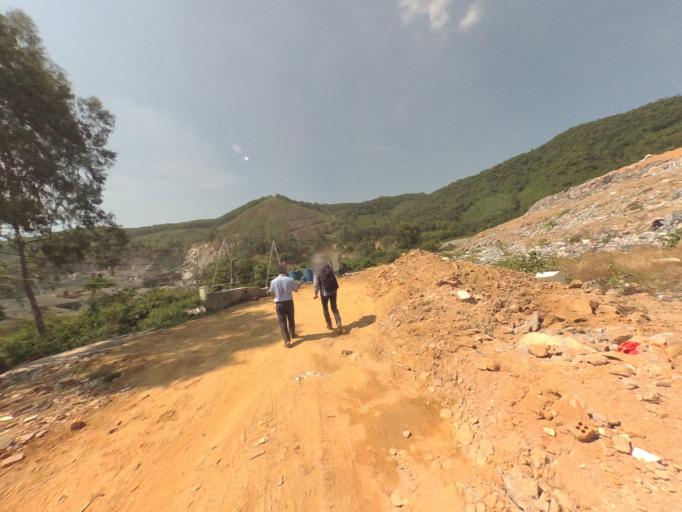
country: VN
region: Da Nang
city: Lien Chieu
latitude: 16.0415
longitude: 108.1437
